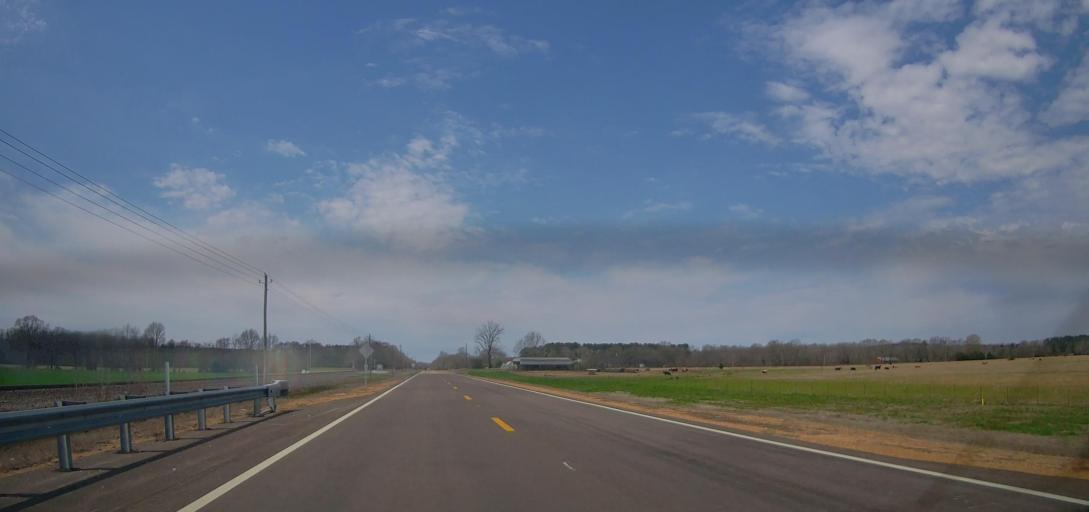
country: US
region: Mississippi
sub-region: Benton County
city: Ashland
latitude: 34.6223
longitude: -89.2382
